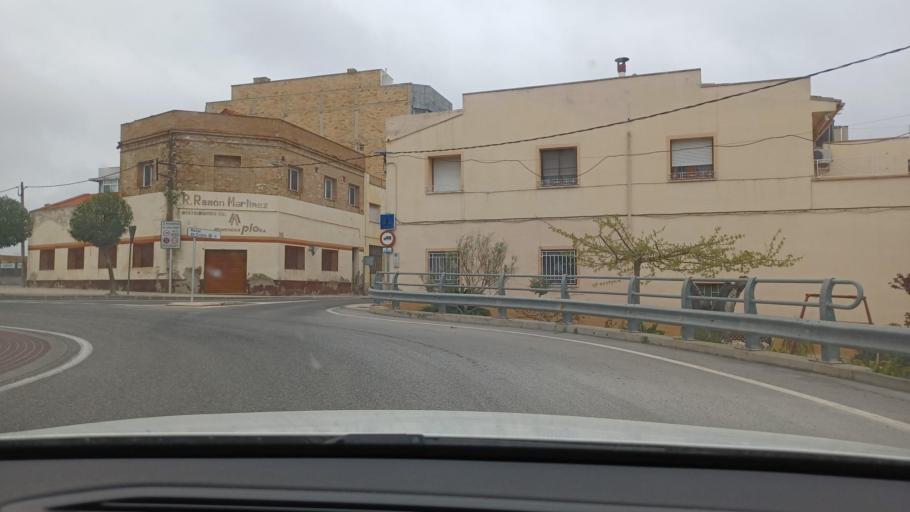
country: ES
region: Catalonia
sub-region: Provincia de Tarragona
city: Tortosa
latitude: 40.8078
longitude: 0.4922
